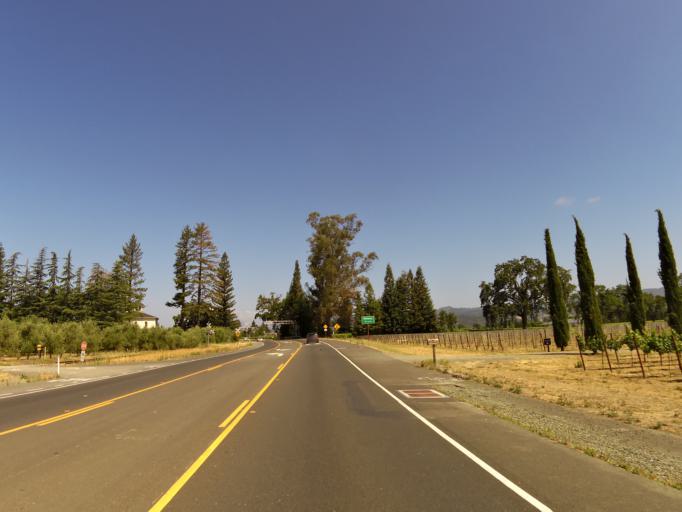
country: US
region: California
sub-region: Napa County
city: Saint Helena
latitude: 38.4756
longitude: -122.4348
